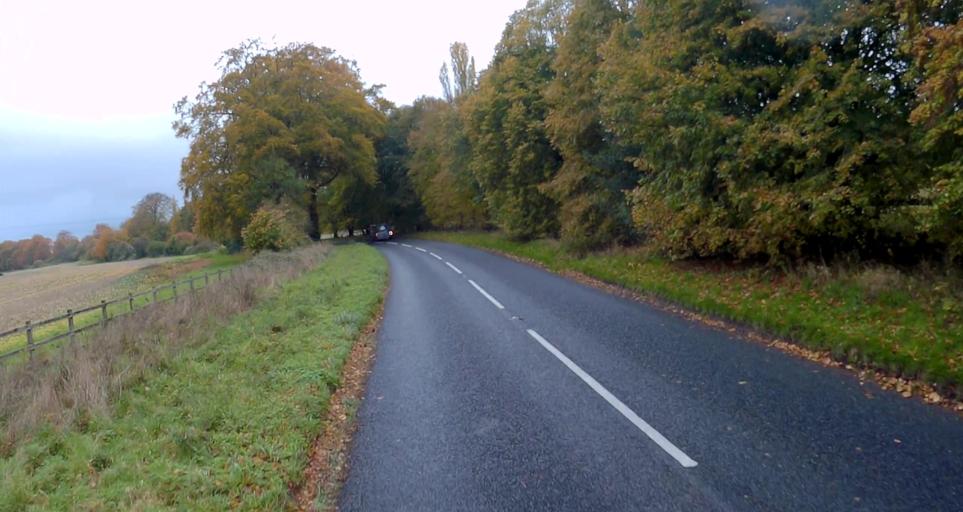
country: GB
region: England
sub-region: Hampshire
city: Kings Worthy
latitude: 51.1237
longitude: -1.1818
